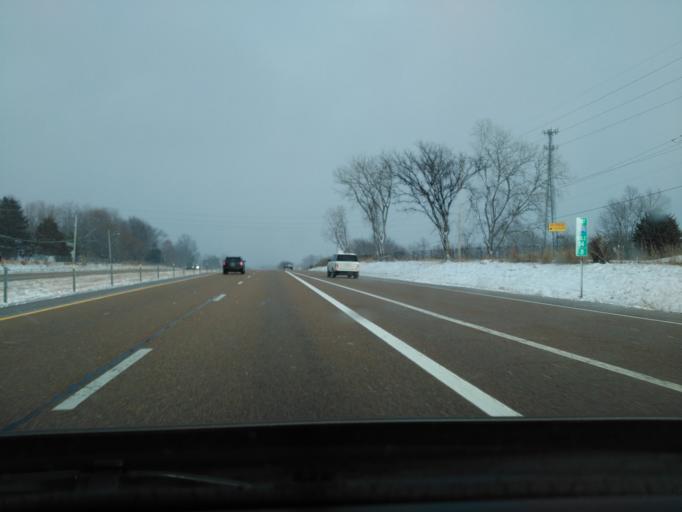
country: US
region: Illinois
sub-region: Madison County
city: Maryville
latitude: 38.7086
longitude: -89.9549
